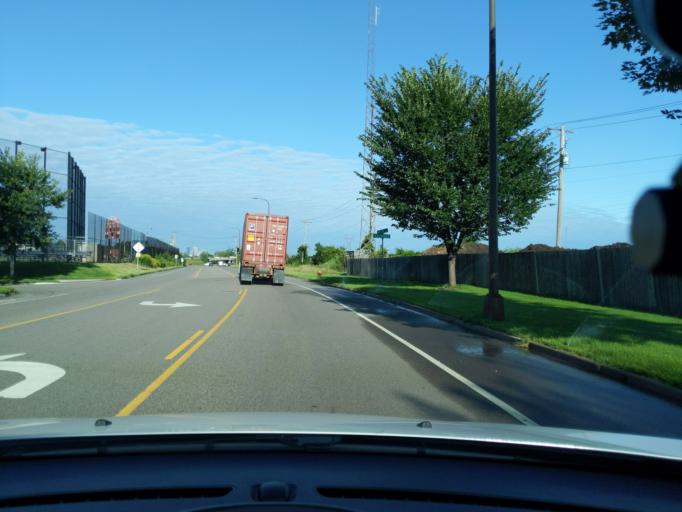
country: US
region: Minnesota
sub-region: Ramsey County
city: Falcon Heights
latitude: 44.9687
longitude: -93.1603
